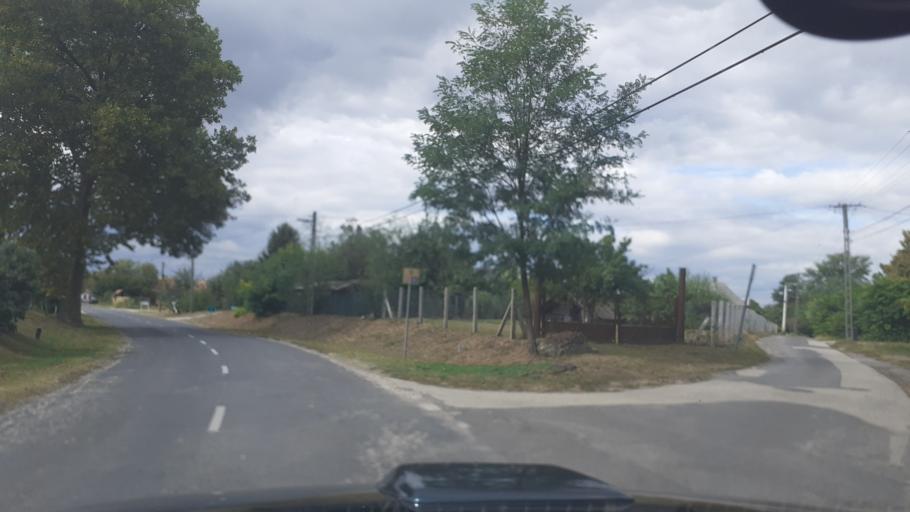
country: HU
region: Bacs-Kiskun
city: Solt
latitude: 46.8127
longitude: 18.9819
